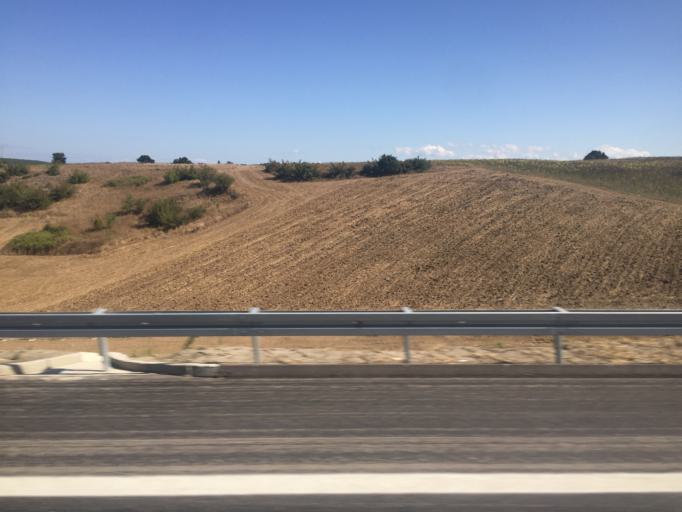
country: TR
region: Bursa
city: Mahmudiye
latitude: 40.2600
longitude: 28.6821
